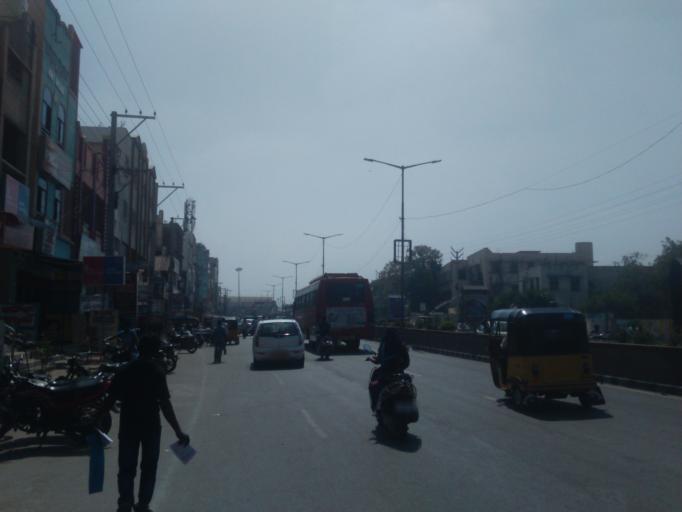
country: IN
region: Telangana
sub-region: Mahbubnagar
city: Alampur
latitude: 15.8205
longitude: 78.0405
